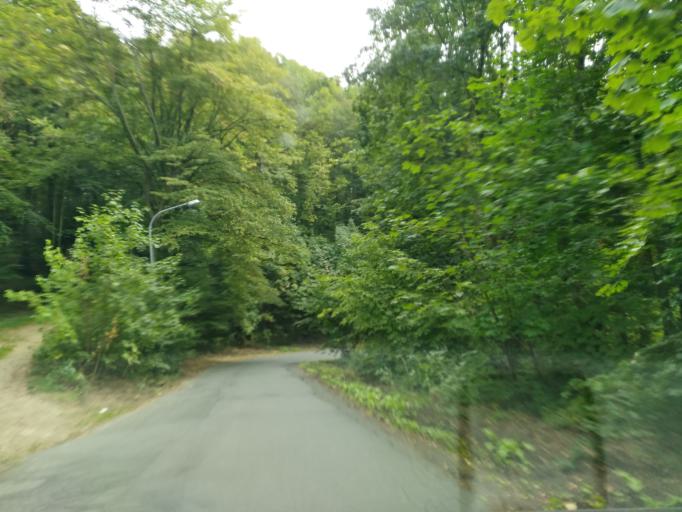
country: DE
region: North Rhine-Westphalia
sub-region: Regierungsbezirk Koln
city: Bad Honnef
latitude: 50.6483
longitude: 7.2383
